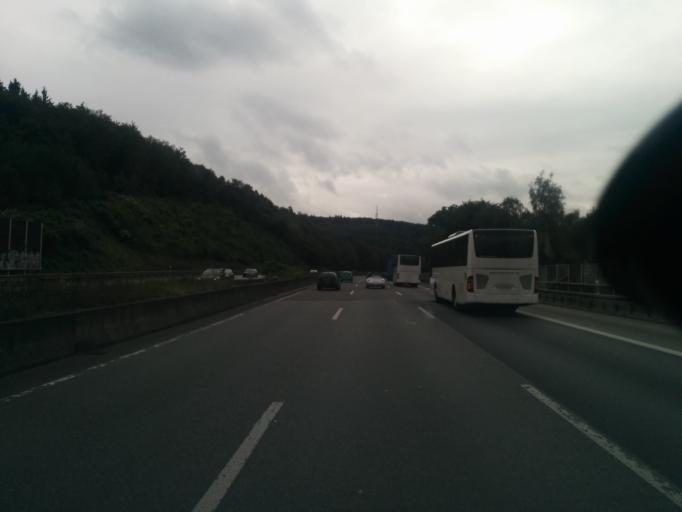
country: DE
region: North Rhine-Westphalia
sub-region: Regierungsbezirk Arnsberg
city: Schwelm
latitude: 51.2705
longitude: 7.2530
